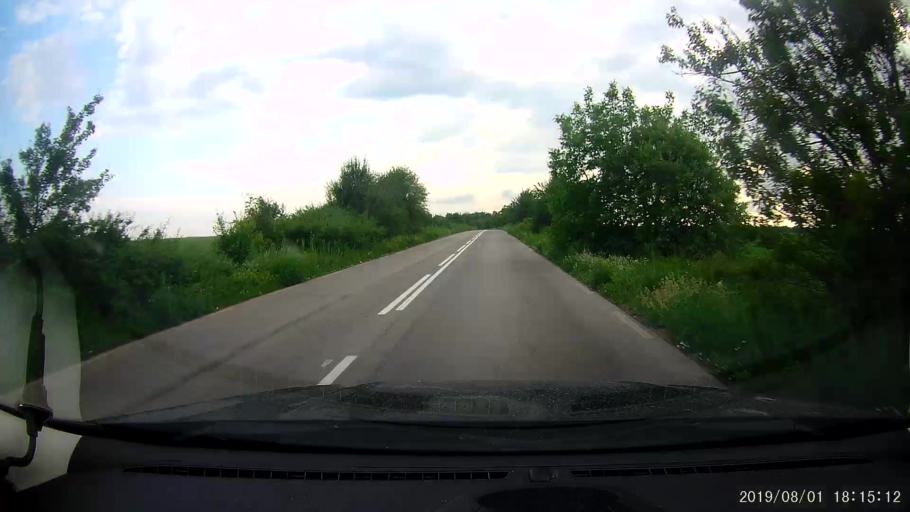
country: BG
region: Silistra
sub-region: Obshtina Dulovo
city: Dulovo
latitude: 43.7573
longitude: 27.1094
